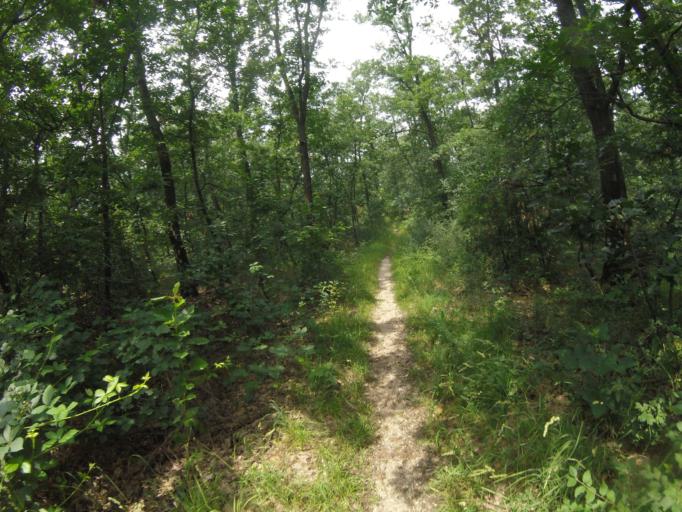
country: HU
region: Pest
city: Toeroekbalint
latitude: 47.4229
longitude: 18.9223
